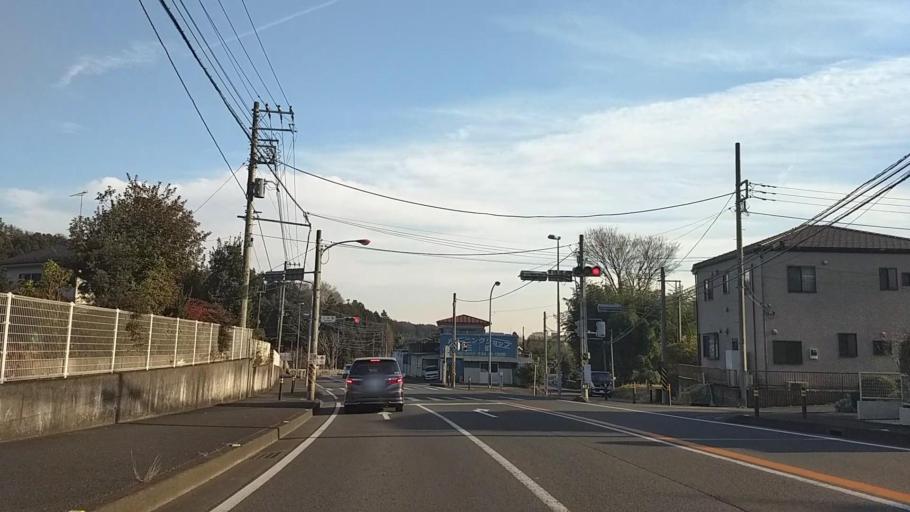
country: JP
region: Kanagawa
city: Zama
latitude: 35.5097
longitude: 139.3044
